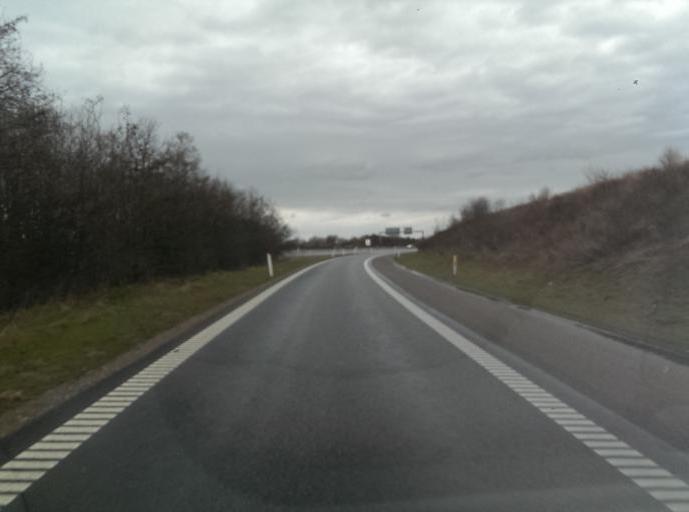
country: DK
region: South Denmark
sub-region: Esbjerg Kommune
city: Esbjerg
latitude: 55.5139
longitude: 8.5087
